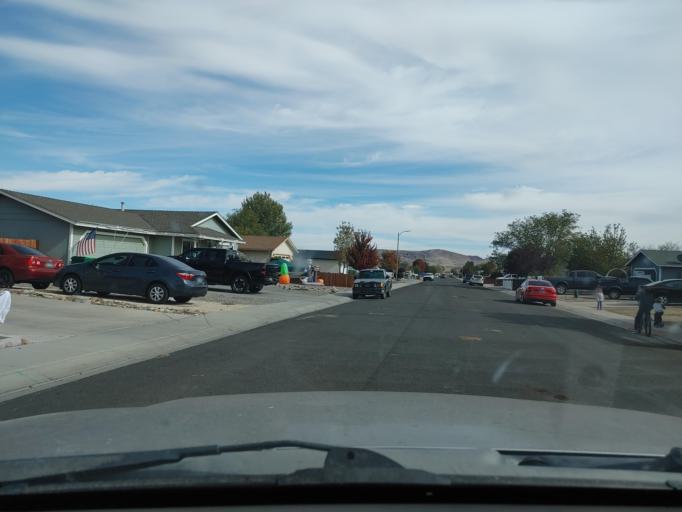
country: US
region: Nevada
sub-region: Lyon County
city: Dayton
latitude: 39.3042
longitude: -119.5415
